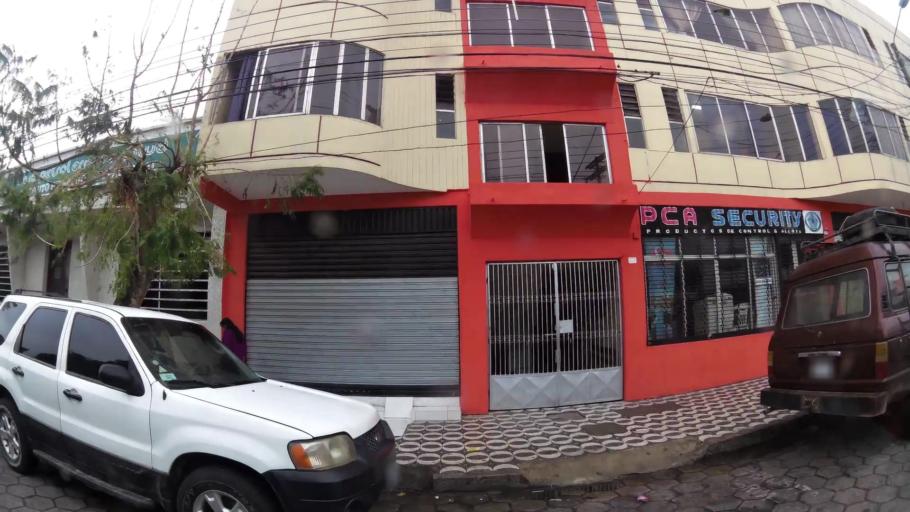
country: BO
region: Santa Cruz
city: Santa Cruz de la Sierra
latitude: -17.7894
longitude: -63.1829
